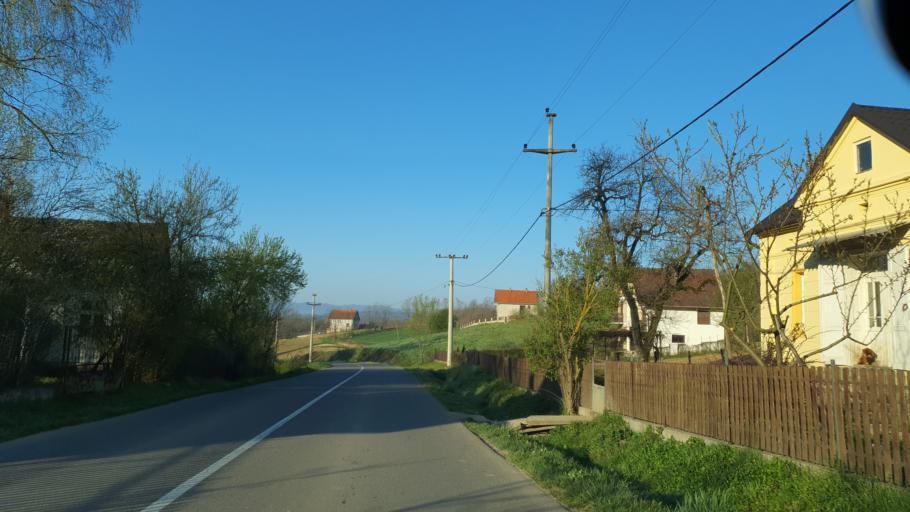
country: RS
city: Bukor
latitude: 44.4642
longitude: 19.4942
